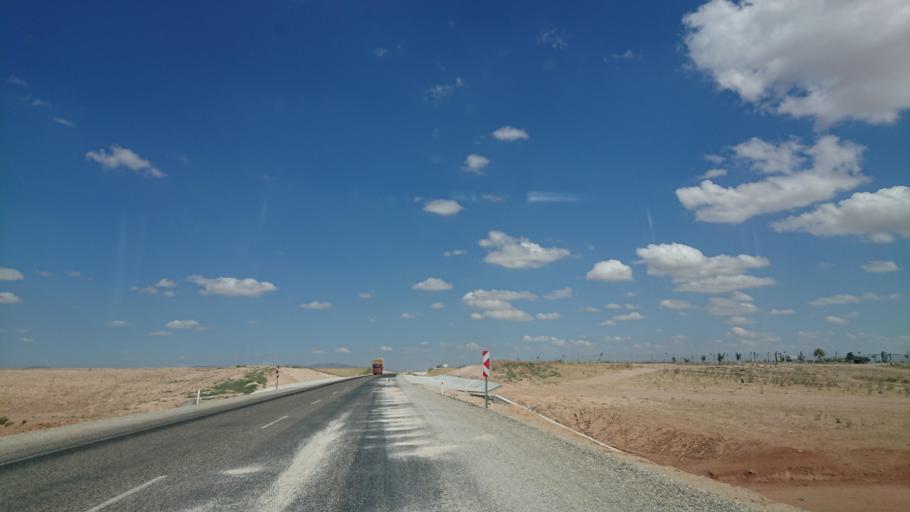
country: TR
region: Kirsehir
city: Kirsehir
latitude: 39.1240
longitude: 33.9918
